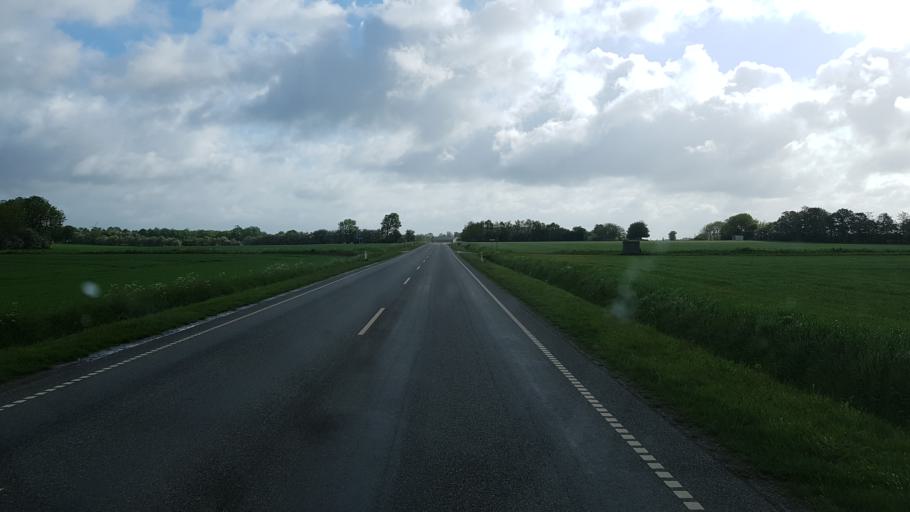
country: DK
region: South Denmark
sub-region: Vejen Kommune
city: Vejen
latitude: 55.4083
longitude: 9.1262
